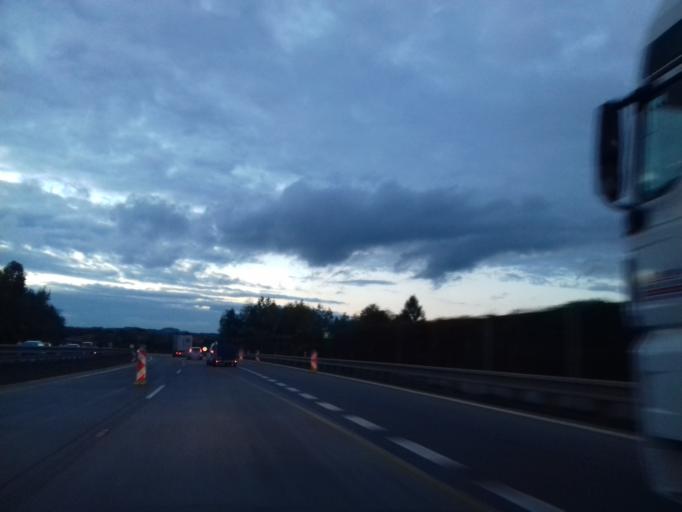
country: CZ
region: Central Bohemia
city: Trhovy Stepanov
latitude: 49.7564
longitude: 14.9693
